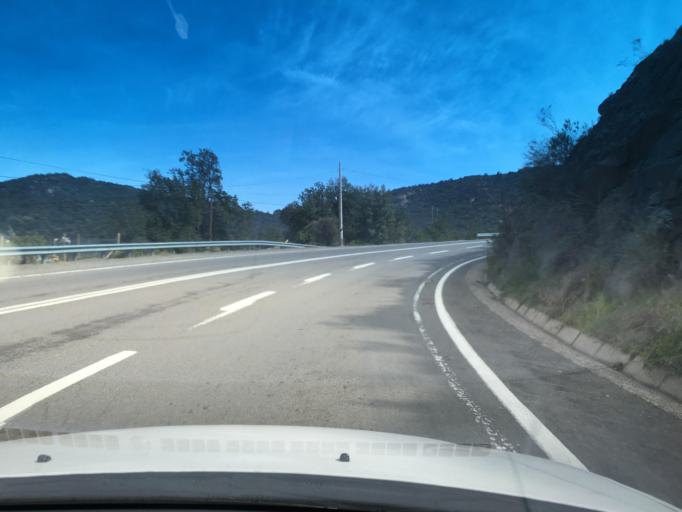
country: CL
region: Valparaiso
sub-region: Provincia de San Felipe
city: Llaillay
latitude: -33.0615
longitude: -70.9982
